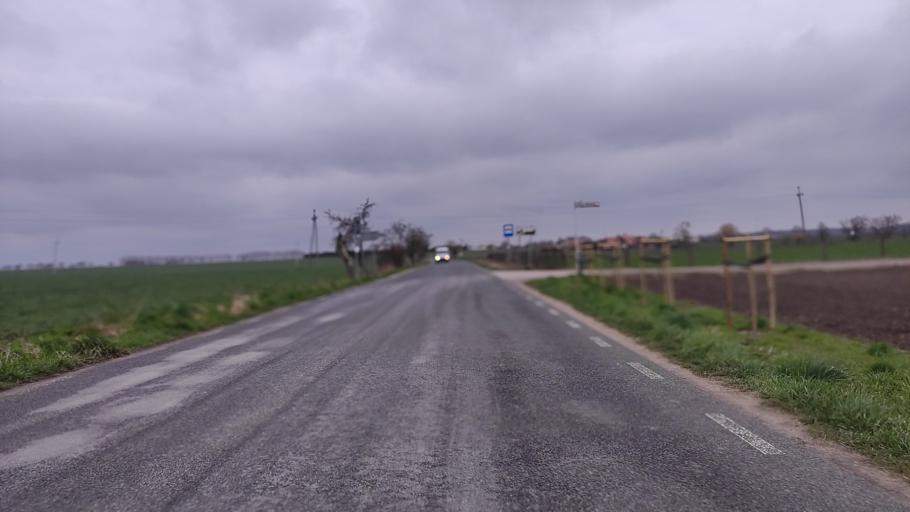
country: PL
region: Greater Poland Voivodeship
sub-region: Powiat poznanski
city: Kostrzyn
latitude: 52.4060
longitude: 17.1654
